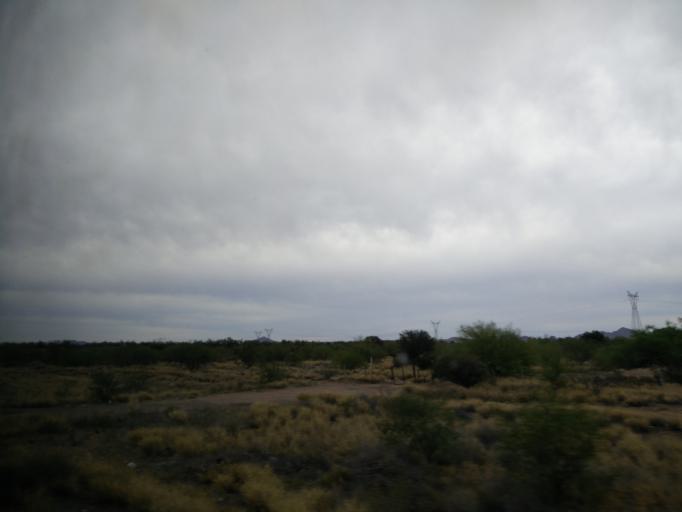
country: MX
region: Sonora
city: Hermosillo
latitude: 28.6512
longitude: -111.0051
